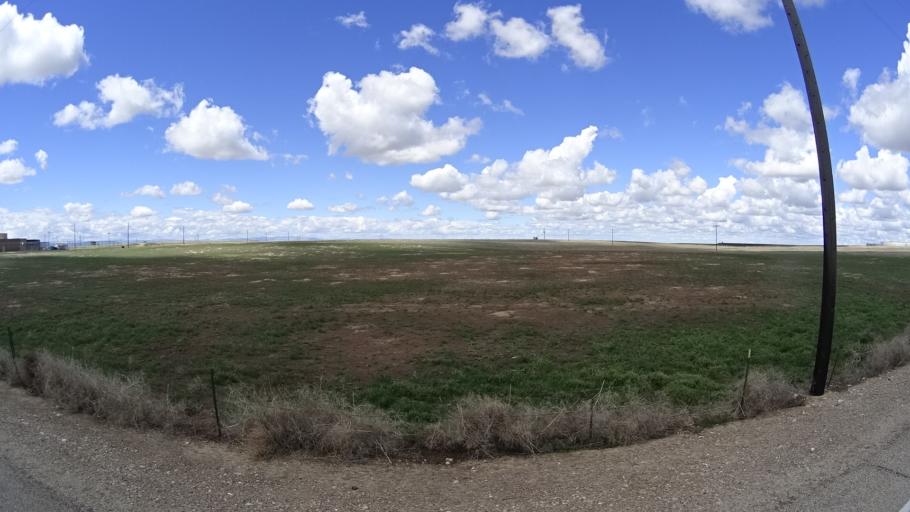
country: US
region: Idaho
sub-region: Ada County
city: Boise
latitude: 43.4638
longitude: -116.2344
